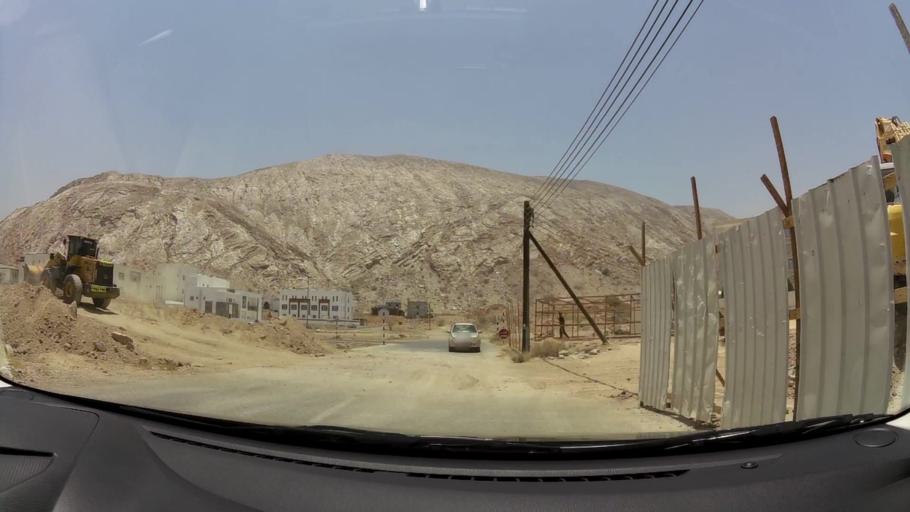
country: OM
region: Muhafazat Masqat
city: Bawshar
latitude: 23.5602
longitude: 58.4182
